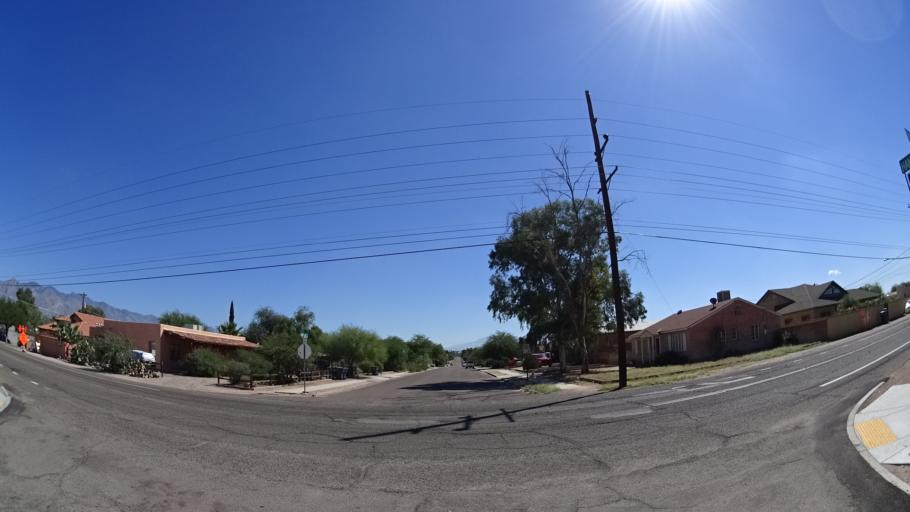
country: US
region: Arizona
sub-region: Pima County
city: Tucson
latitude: 32.2478
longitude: -110.9570
